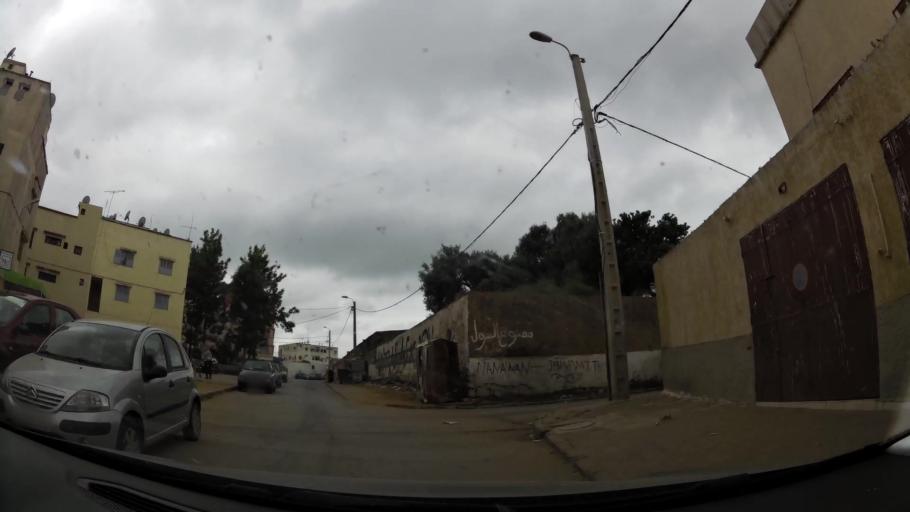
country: MA
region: Rabat-Sale-Zemmour-Zaer
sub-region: Rabat
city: Rabat
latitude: 33.9976
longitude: -6.8131
